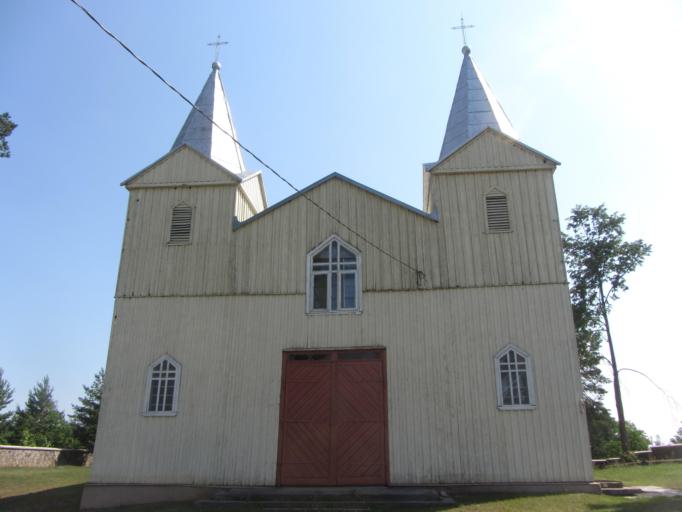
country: LT
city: Veisiejai
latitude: 54.1641
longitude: 23.6429
